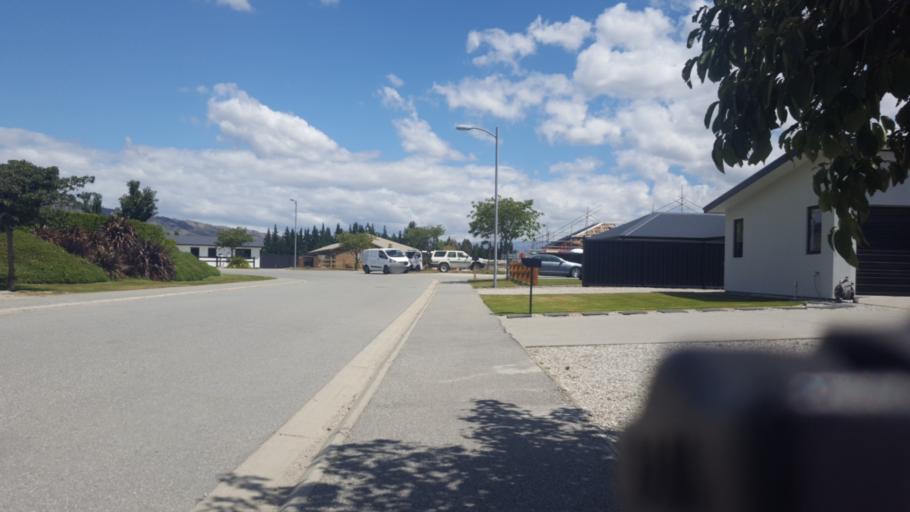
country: NZ
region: Otago
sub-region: Queenstown-Lakes District
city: Wanaka
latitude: -44.9811
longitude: 169.2349
